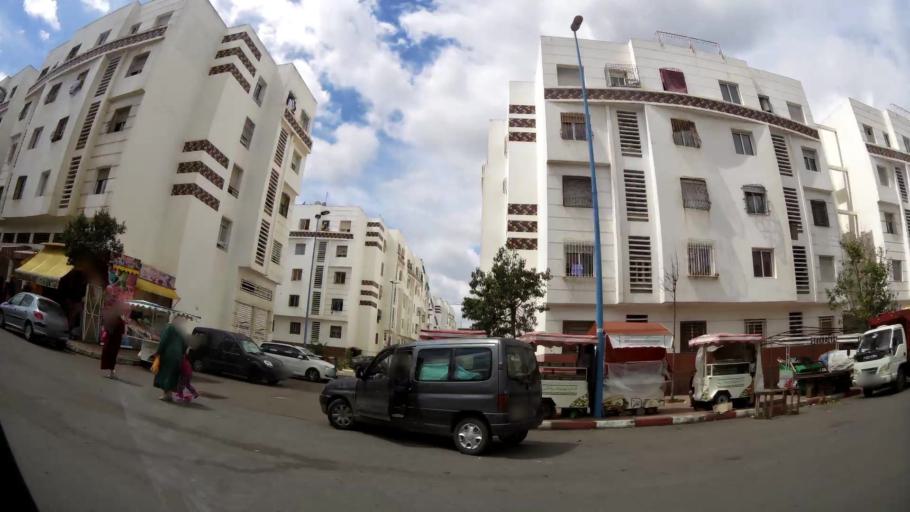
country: MA
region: Grand Casablanca
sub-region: Casablanca
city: Casablanca
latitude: 33.6102
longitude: -7.5432
